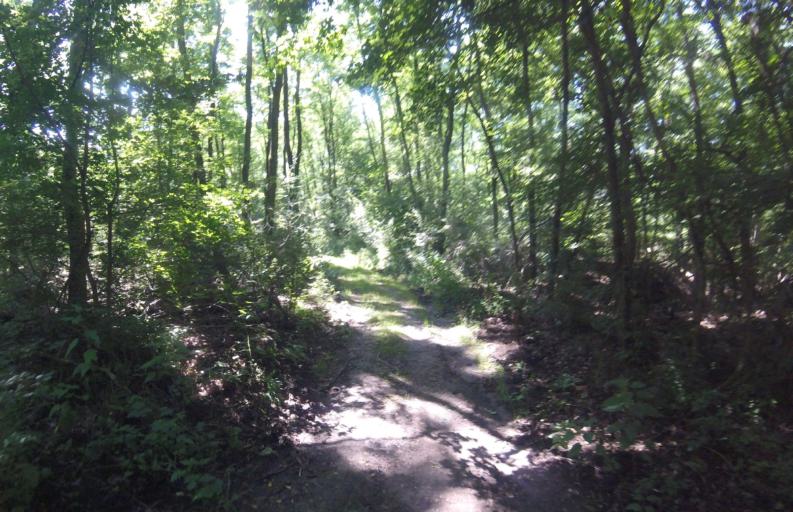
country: HU
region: Pest
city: Szob
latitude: 47.8786
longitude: 18.8726
